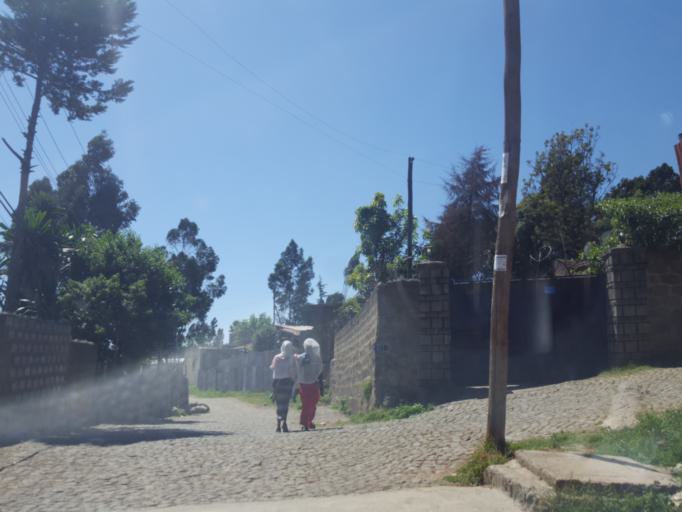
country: ET
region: Adis Abeba
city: Addis Ababa
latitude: 9.0591
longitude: 38.7455
